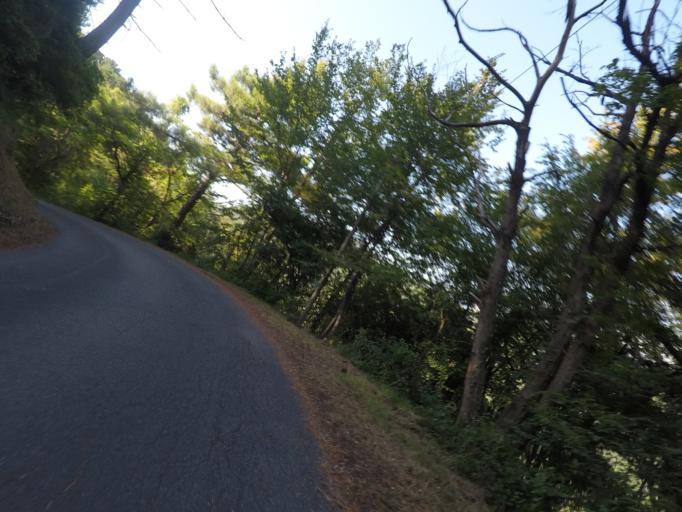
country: IT
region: Tuscany
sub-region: Provincia di Massa-Carrara
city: Carrara
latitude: 44.0808
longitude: 10.0655
